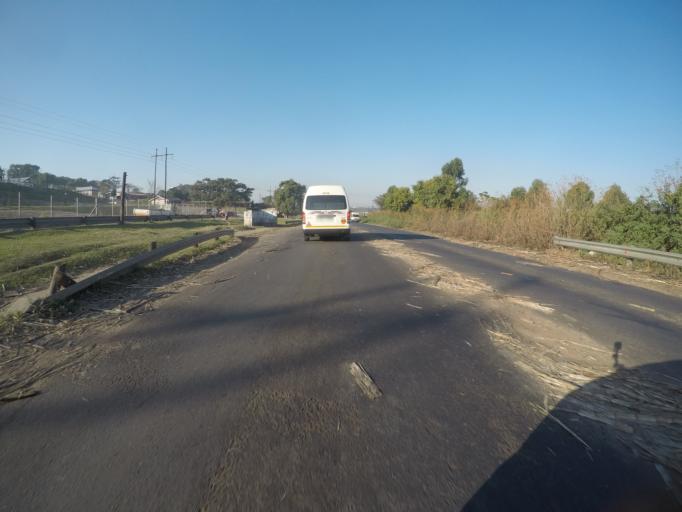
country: ZA
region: KwaZulu-Natal
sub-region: iLembe District Municipality
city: Stanger
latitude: -29.3906
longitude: 31.2510
